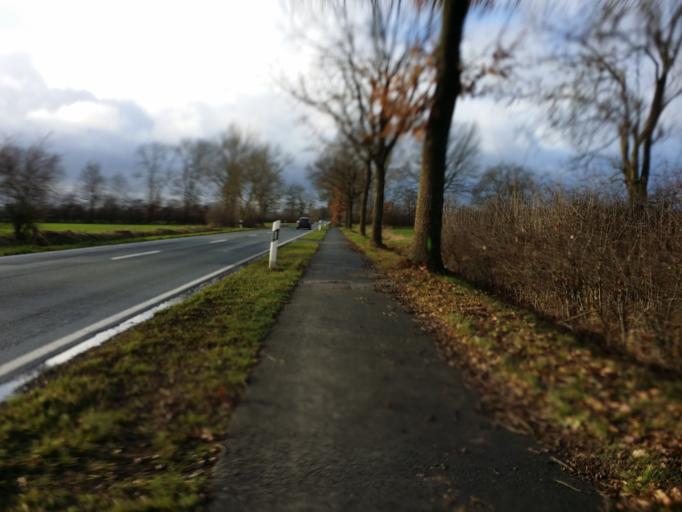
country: DE
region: Lower Saxony
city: Riede
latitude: 52.9850
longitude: 8.9453
